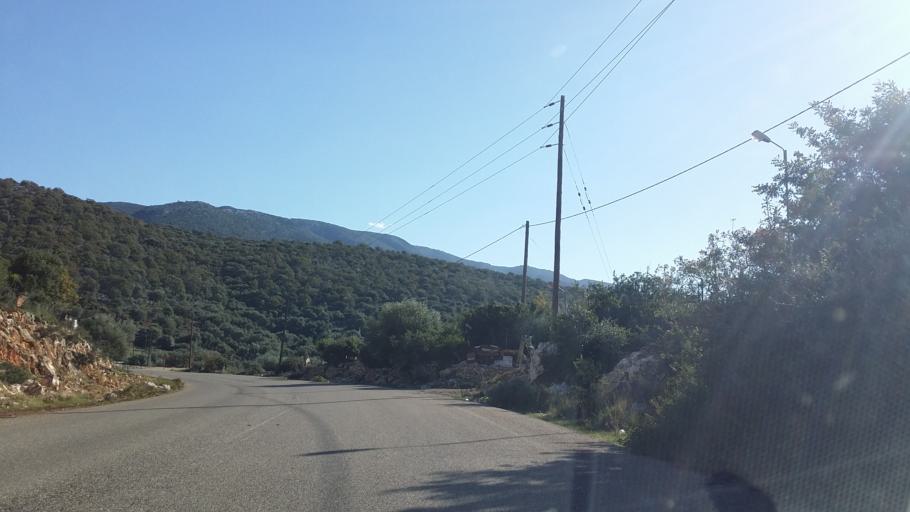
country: GR
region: West Greece
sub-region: Nomos Aitolias kai Akarnanias
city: Astakos
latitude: 38.6052
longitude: 21.0236
